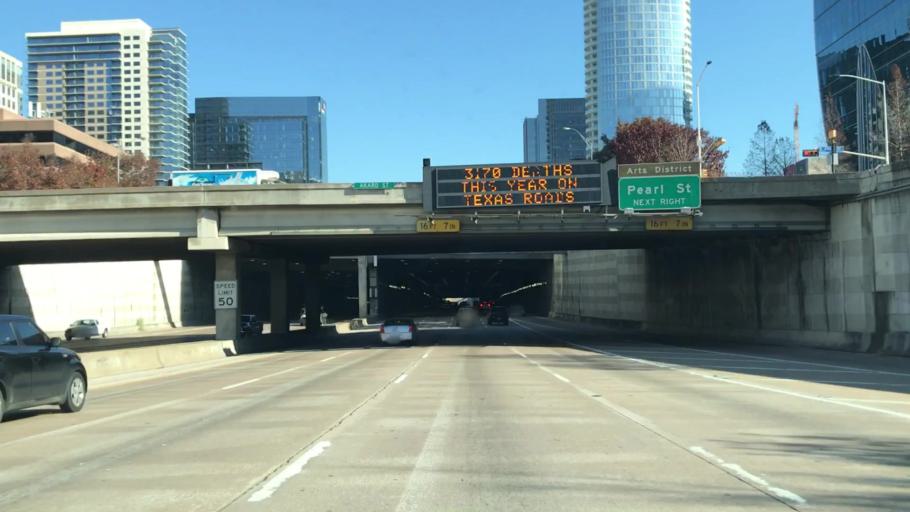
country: US
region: Texas
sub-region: Dallas County
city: Dallas
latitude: 32.7875
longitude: -96.8037
